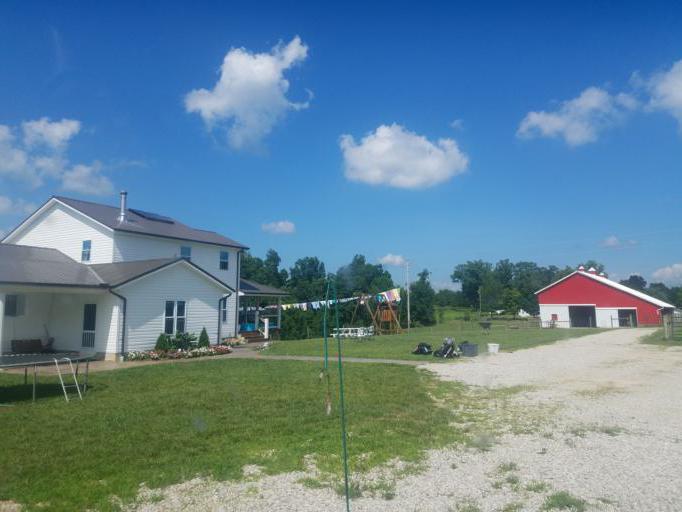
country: US
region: Kentucky
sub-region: Barren County
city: Cave City
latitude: 37.2718
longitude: -86.0702
